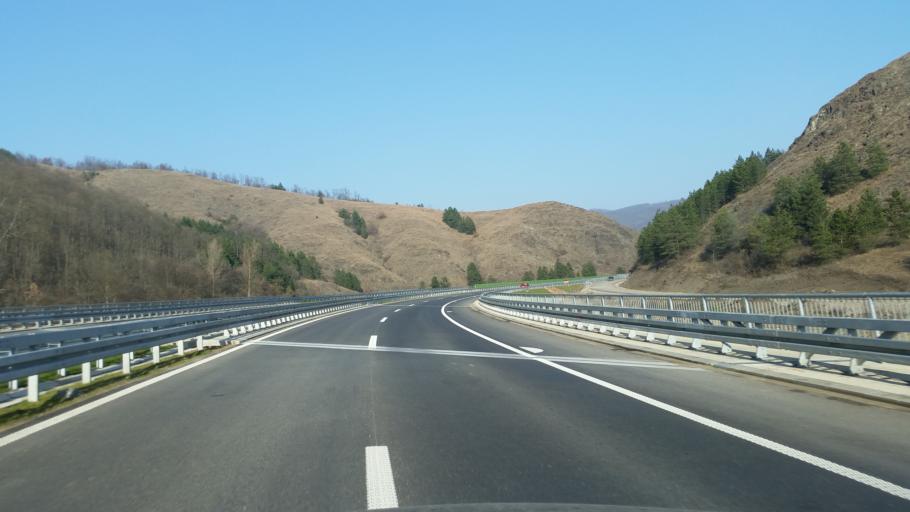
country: RS
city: Prislonica
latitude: 43.9903
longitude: 20.3995
